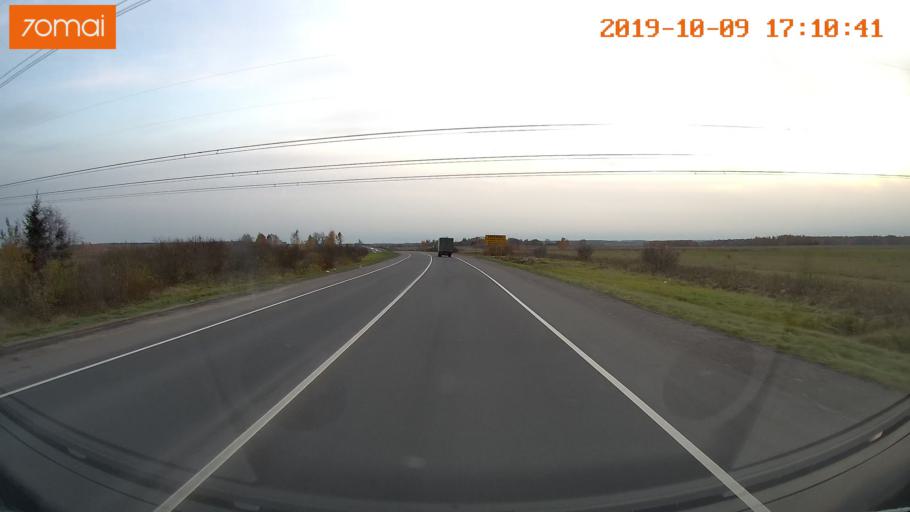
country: RU
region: Ivanovo
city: Privolzhsk
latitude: 57.3525
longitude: 41.2559
